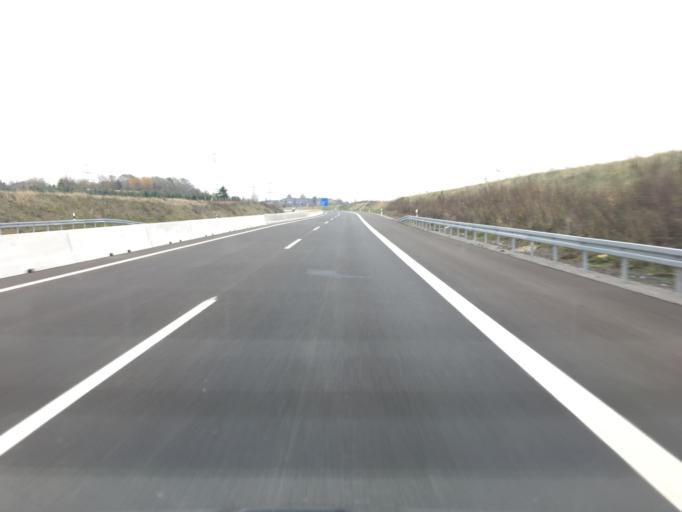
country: DE
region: North Rhine-Westphalia
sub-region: Regierungsbezirk Dusseldorf
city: Heiligenhaus
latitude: 51.3226
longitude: 7.0014
